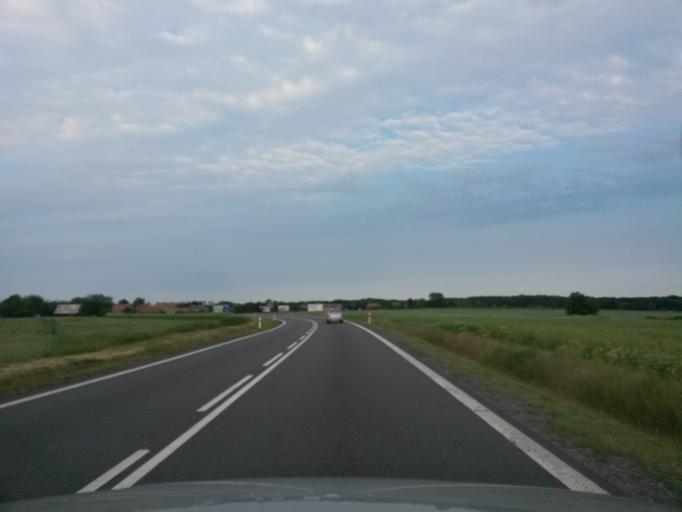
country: PL
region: Lower Silesian Voivodeship
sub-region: Powiat swidnicki
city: Zarow
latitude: 51.0068
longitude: 16.5415
